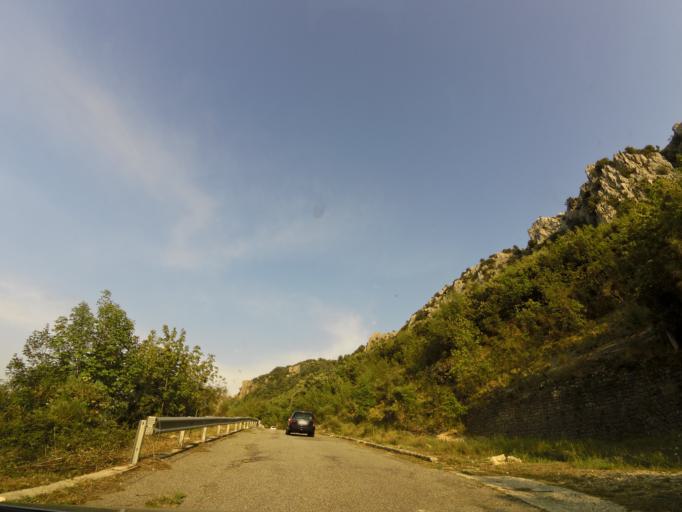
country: IT
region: Calabria
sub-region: Provincia di Reggio Calabria
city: Pazzano
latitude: 38.4655
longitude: 16.4336
